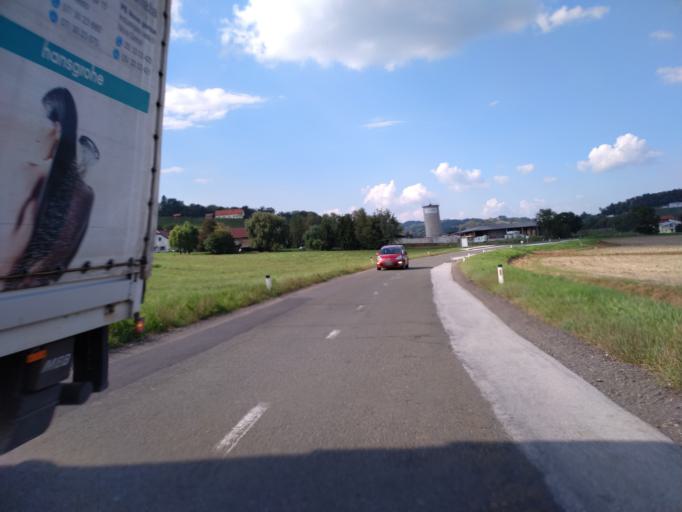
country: SI
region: Pesnica
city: Pesnica pri Mariboru
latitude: 46.5982
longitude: 15.6577
